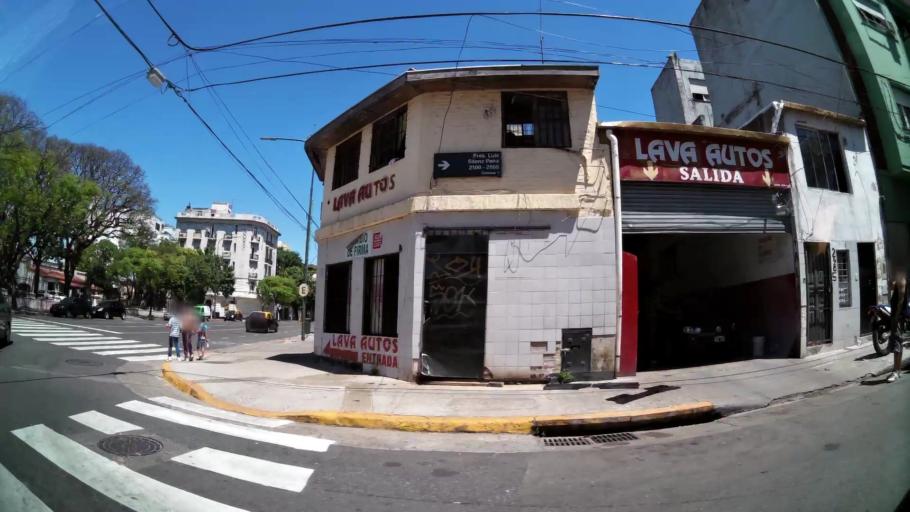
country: AR
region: Buenos Aires F.D.
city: Buenos Aires
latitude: -34.6330
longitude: -58.3865
